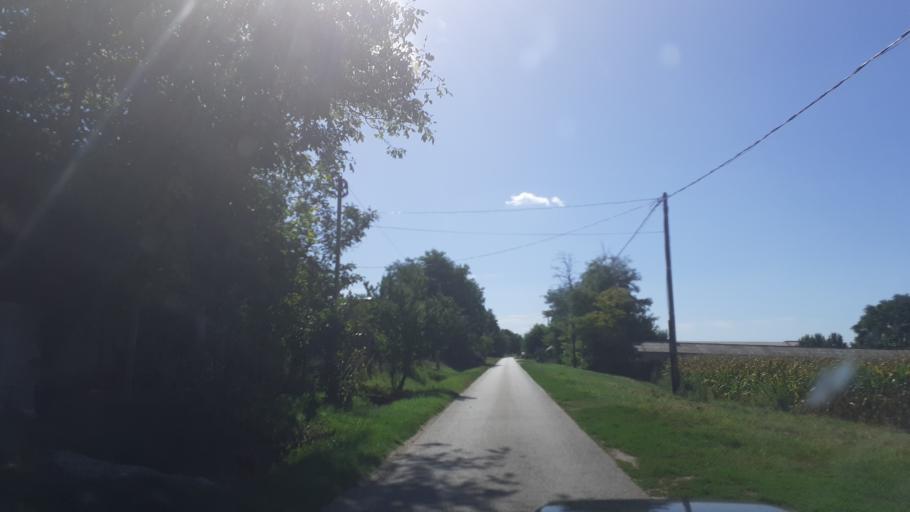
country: HU
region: Fejer
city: Baracska
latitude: 47.2788
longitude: 18.7747
